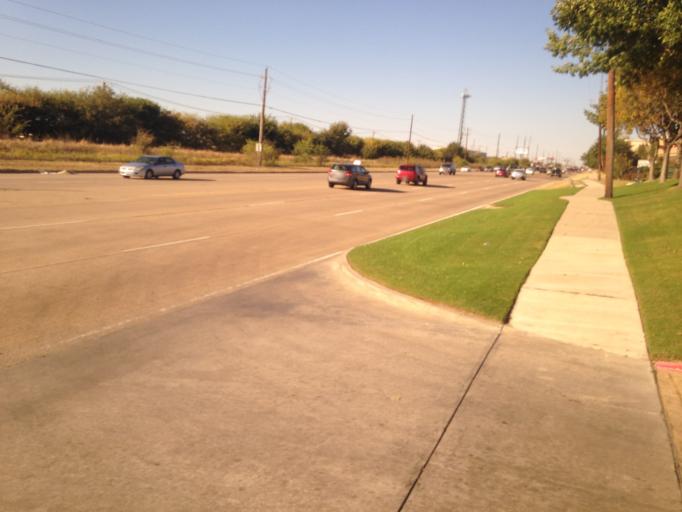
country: US
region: Texas
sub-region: Tarrant County
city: Keller
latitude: 32.9019
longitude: -97.2574
